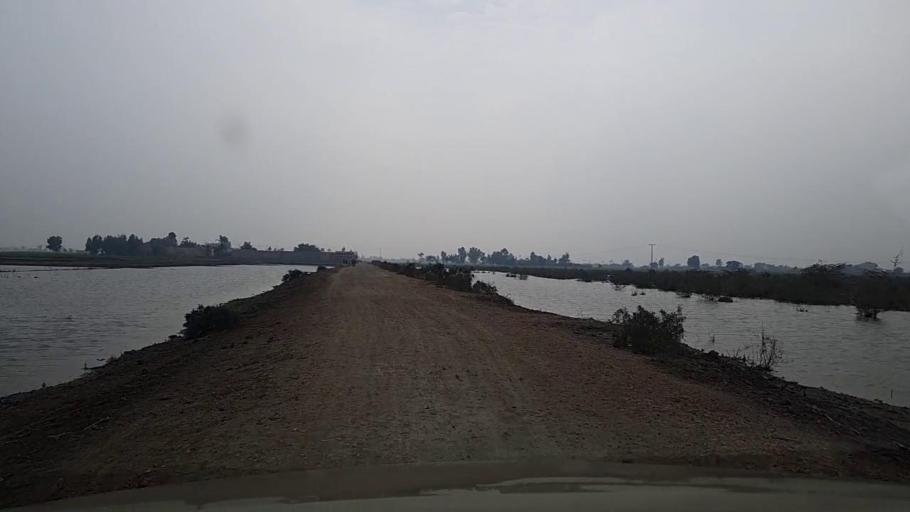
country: PK
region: Sindh
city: Sanghar
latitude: 26.1188
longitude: 68.9164
